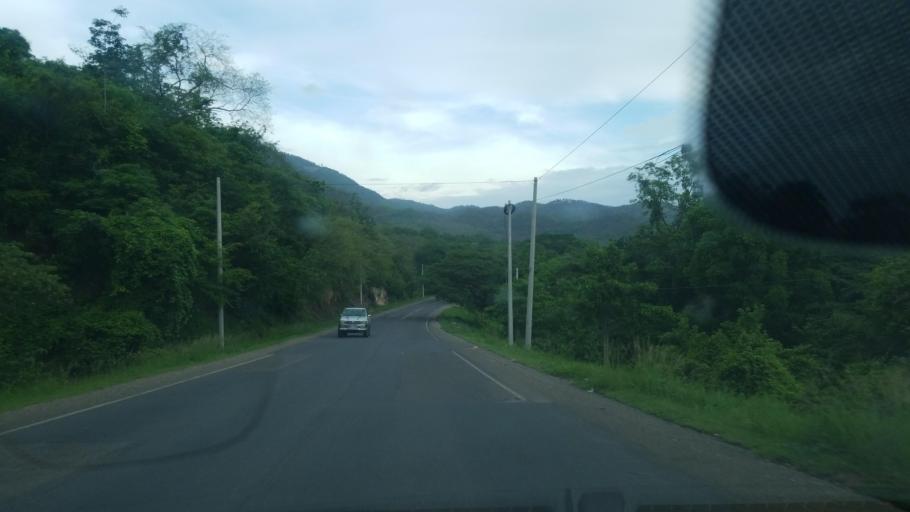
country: HN
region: Santa Barbara
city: Santa Barbara
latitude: 14.8925
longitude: -88.2502
